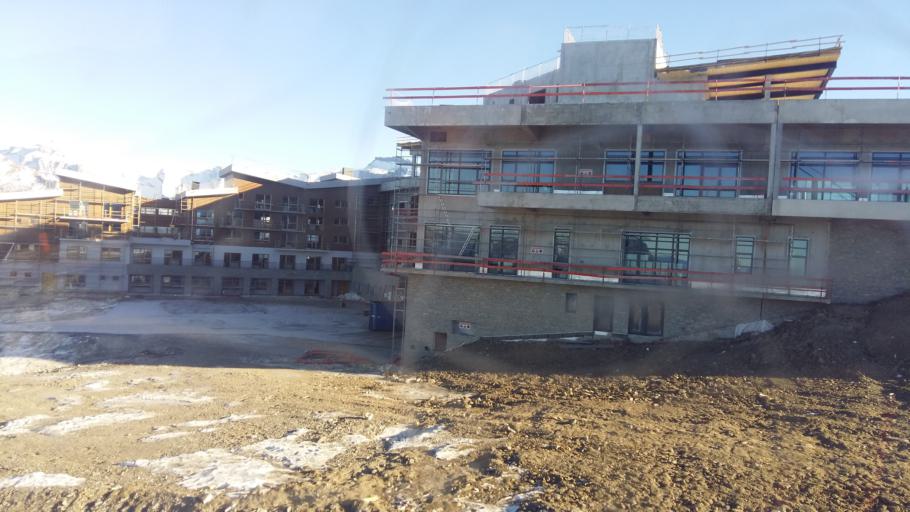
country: FR
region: Rhone-Alpes
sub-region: Departement de la Haute-Savoie
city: Samoens
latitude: 46.0563
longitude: 6.7029
